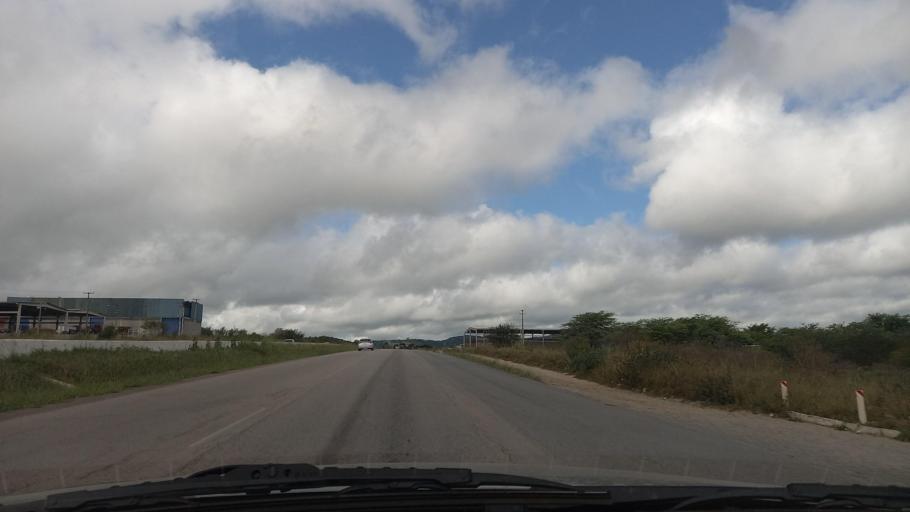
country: BR
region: Pernambuco
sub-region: Caruaru
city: Caruaru
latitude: -8.3108
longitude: -35.9905
